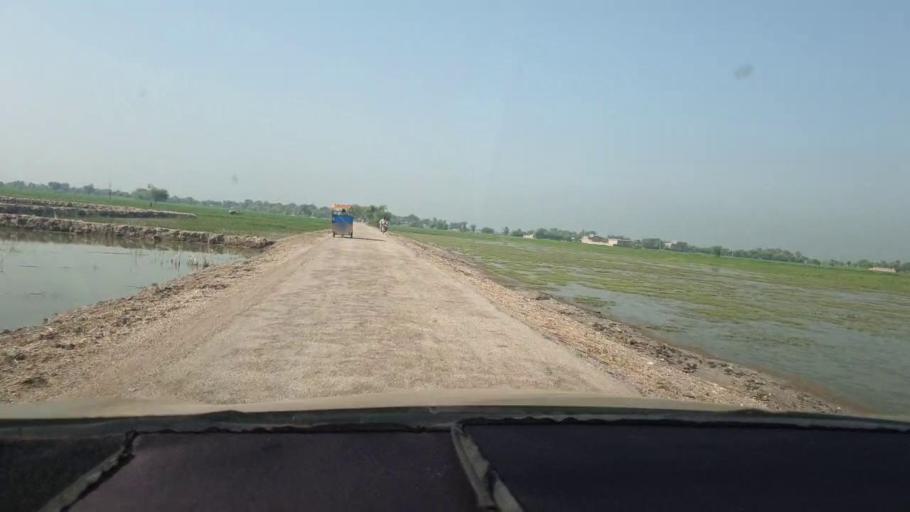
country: PK
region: Sindh
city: Kambar
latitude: 27.5757
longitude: 68.0882
